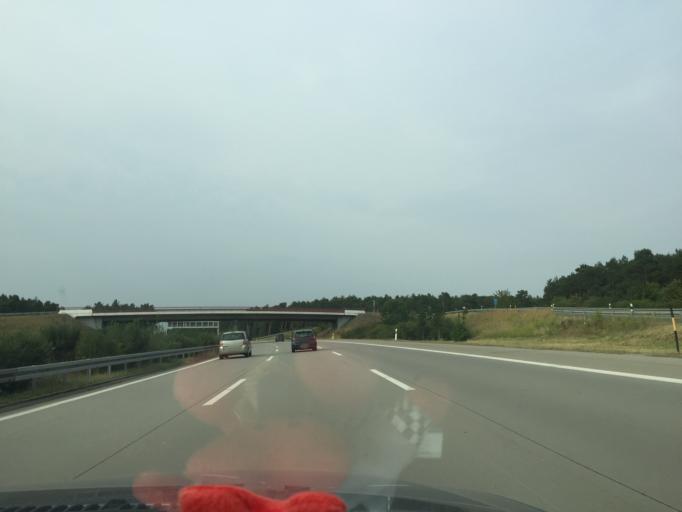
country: DE
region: Brandenburg
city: Grunheide
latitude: 52.3874
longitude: 13.7862
